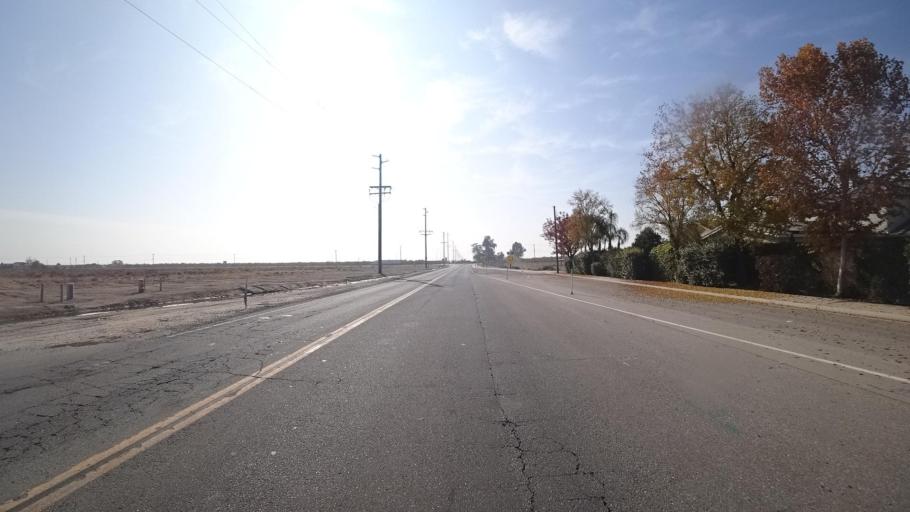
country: US
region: California
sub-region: Kern County
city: Delano
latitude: 35.7638
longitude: -119.2232
